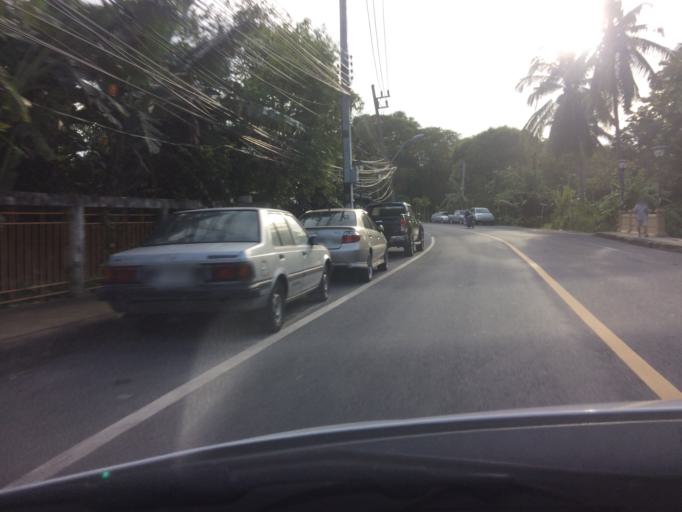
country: TH
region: Phuket
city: Phuket
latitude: 7.8909
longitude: 98.3996
